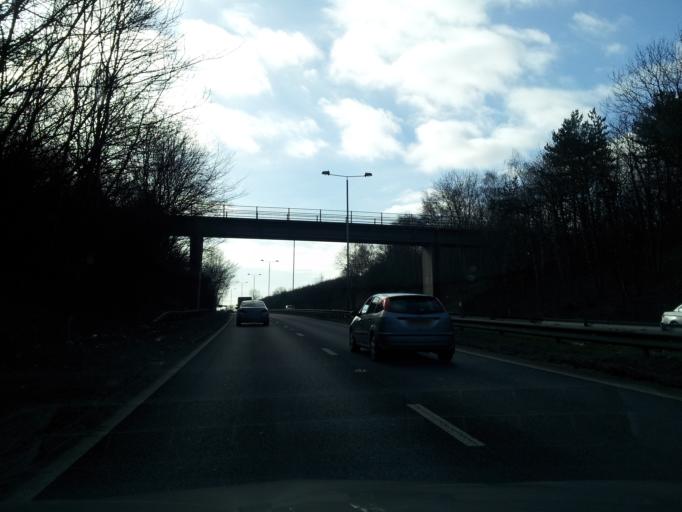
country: GB
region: England
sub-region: Derbyshire
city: Long Eaton
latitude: 52.9289
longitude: -1.2571
